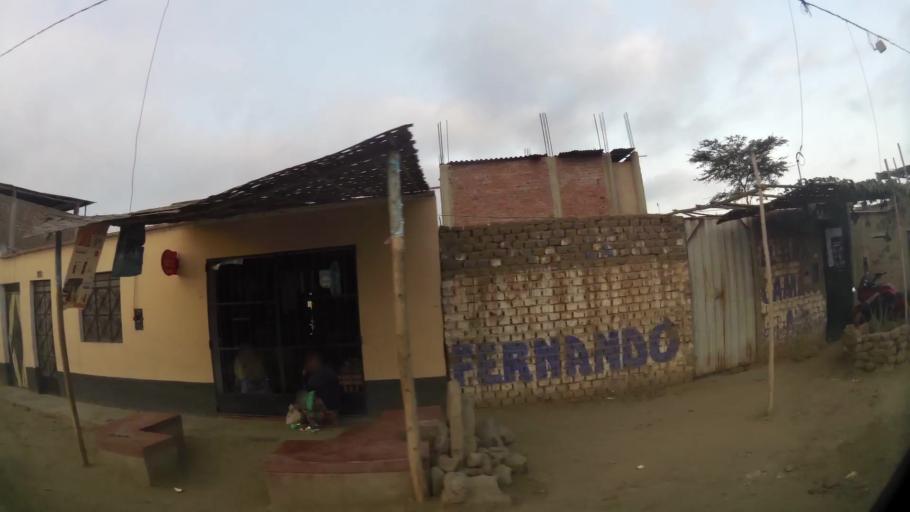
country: PE
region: La Libertad
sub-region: Provincia de Trujillo
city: El Porvenir
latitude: -8.0641
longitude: -79.0087
